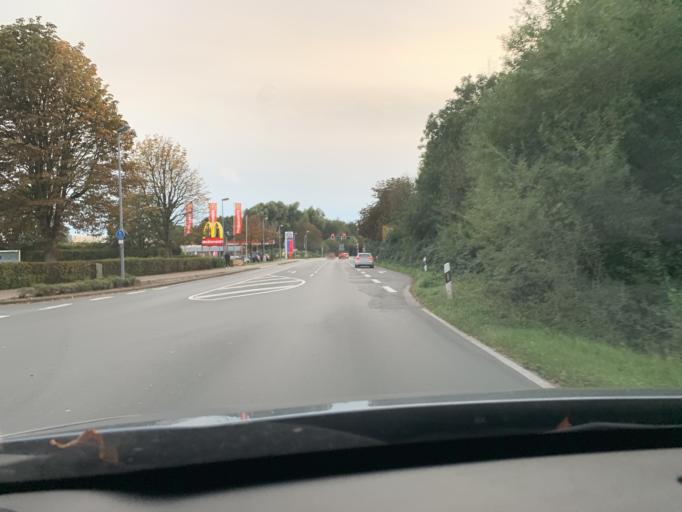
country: DE
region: Lower Saxony
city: Westerstede
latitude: 53.2532
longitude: 7.9325
